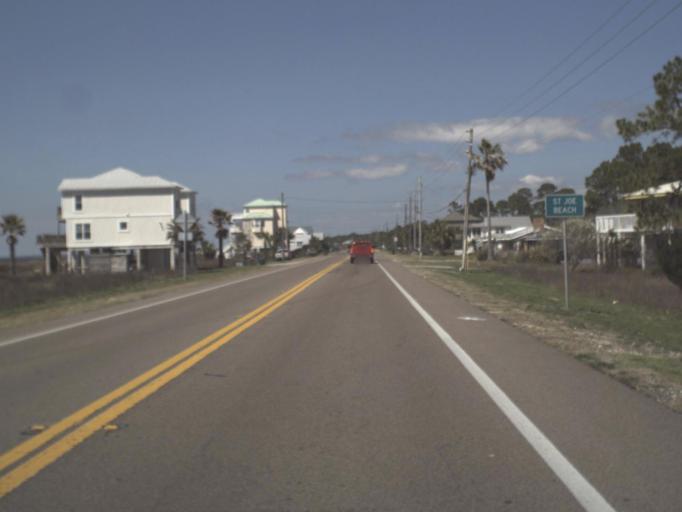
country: US
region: Florida
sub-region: Bay County
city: Mexico Beach
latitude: 29.8928
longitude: -85.3585
